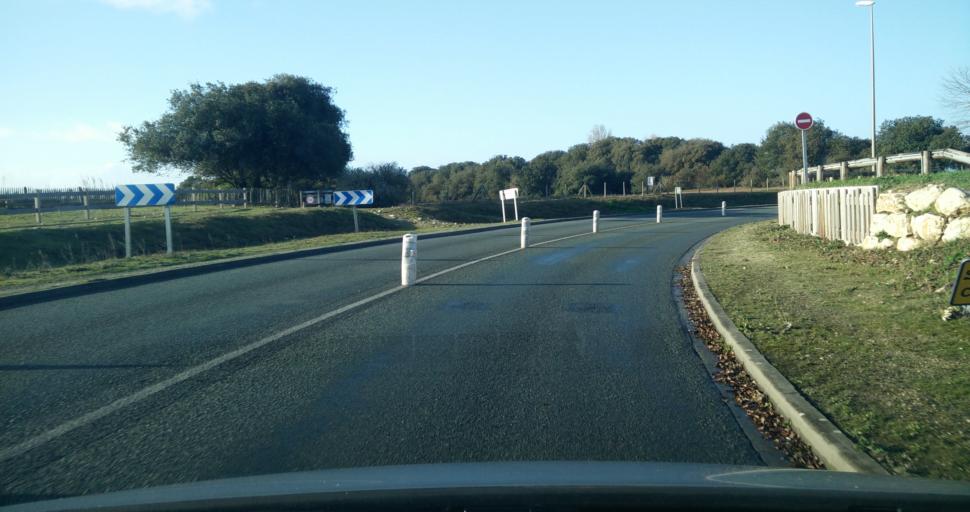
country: FR
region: Poitou-Charentes
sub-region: Departement de la Charente-Maritime
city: Rivedoux-Plage
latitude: 46.1508
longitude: -1.2748
